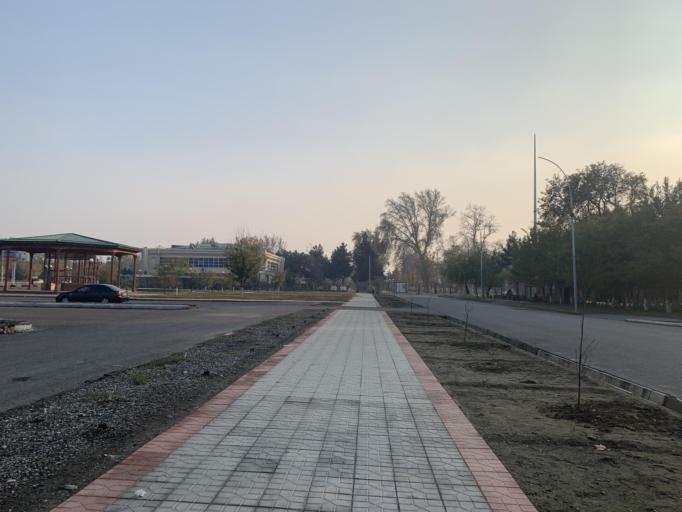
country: UZ
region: Fergana
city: Qo`qon
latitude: 40.5389
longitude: 70.9353
